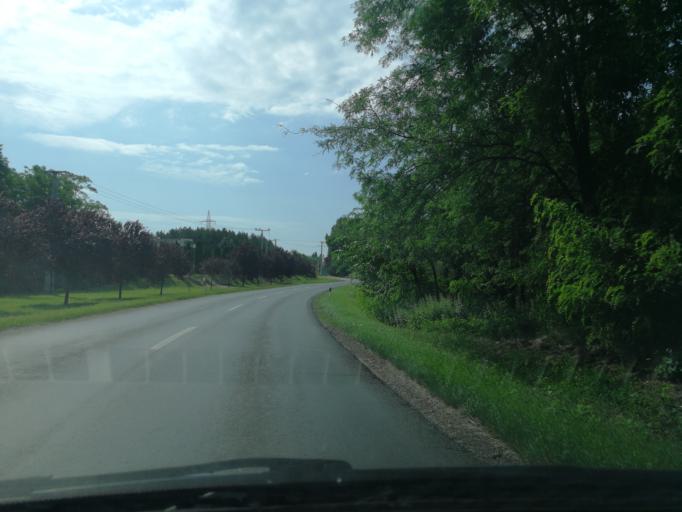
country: HU
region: Bacs-Kiskun
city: Nagybaracska
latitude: 46.0407
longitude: 18.9224
